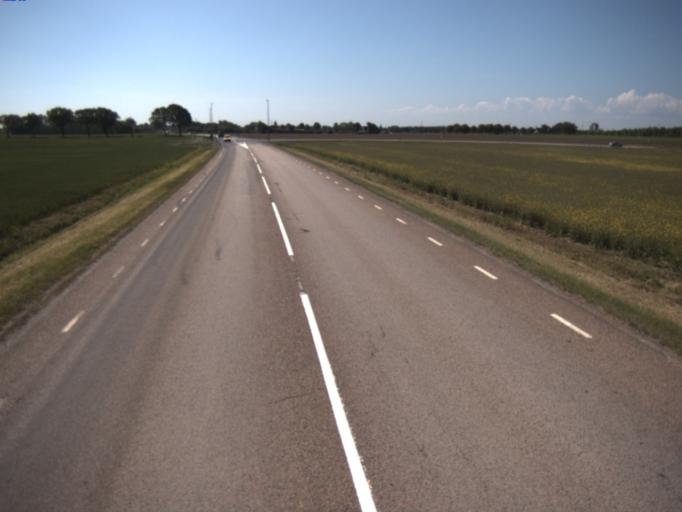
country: SE
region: Skane
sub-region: Helsingborg
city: Barslov
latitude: 56.0312
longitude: 12.7906
